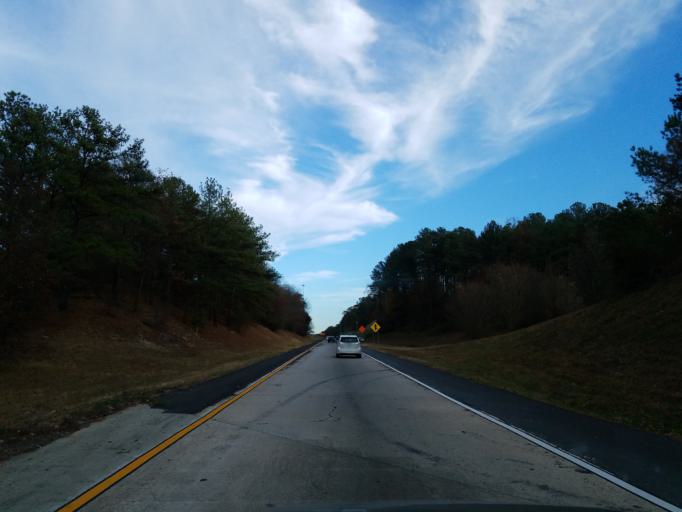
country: US
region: Georgia
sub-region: Fulton County
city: East Point
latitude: 33.7617
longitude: -84.4910
